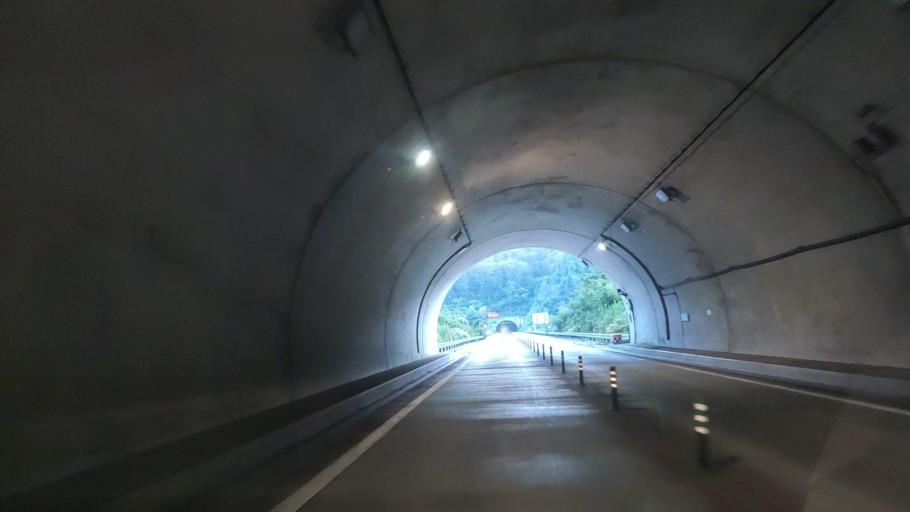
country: JP
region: Toyama
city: Himi
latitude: 36.9341
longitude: 137.0157
